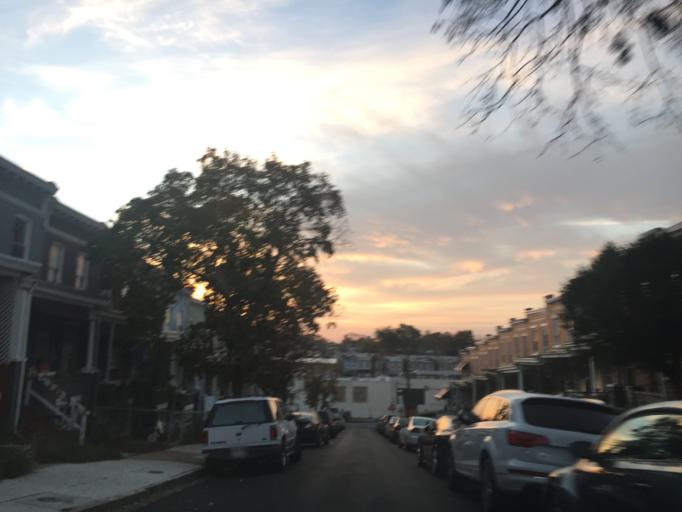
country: US
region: Maryland
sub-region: City of Baltimore
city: Baltimore
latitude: 39.3158
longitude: -76.6058
